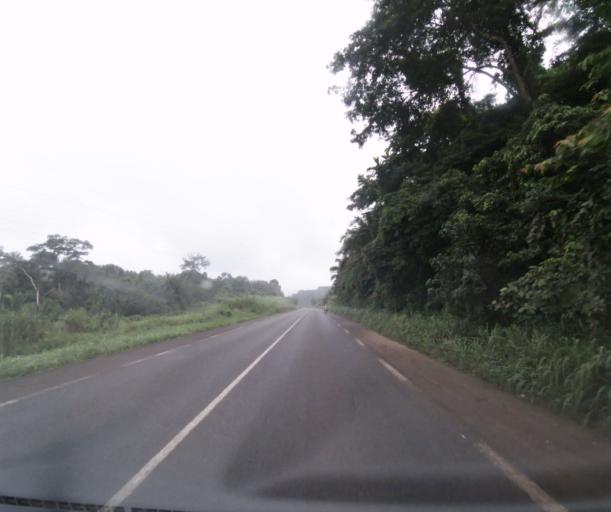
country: CM
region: Centre
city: Eseka
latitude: 3.8827
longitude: 10.6993
